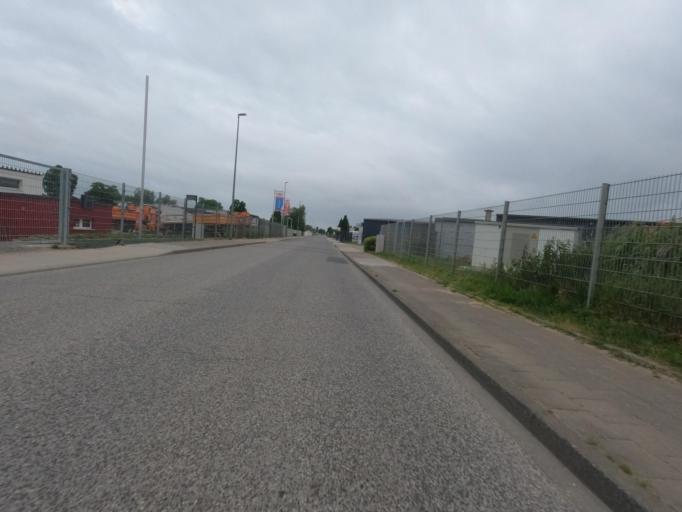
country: DE
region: North Rhine-Westphalia
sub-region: Regierungsbezirk Koln
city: Wassenberg
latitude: 51.0989
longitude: 6.1417
